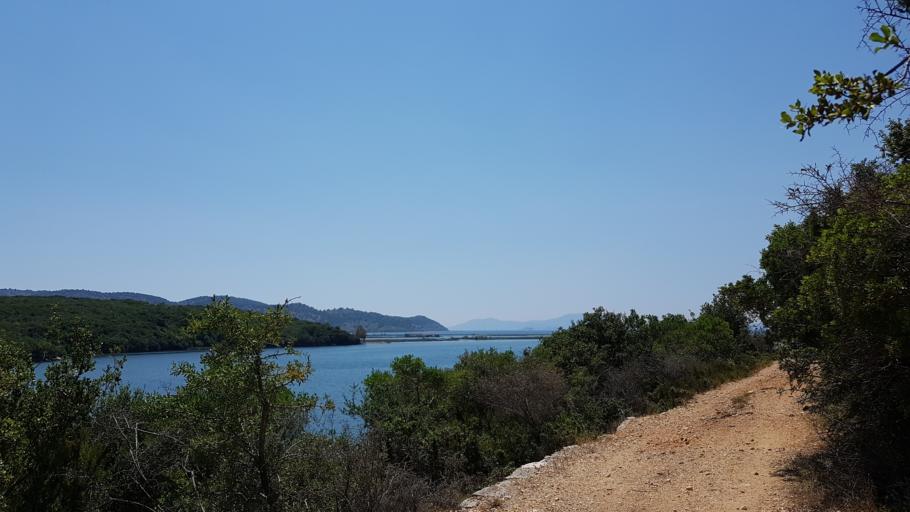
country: AL
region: Vlore
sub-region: Rrethi i Sarandes
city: Xarre
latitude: 39.7501
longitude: 19.9947
